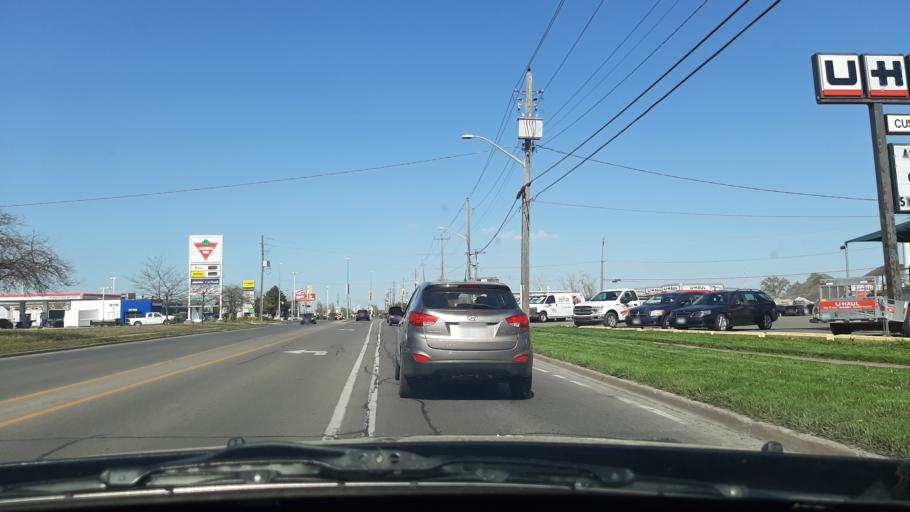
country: CA
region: Ontario
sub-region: Regional Municipality of Niagara
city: St. Catharines
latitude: 43.1741
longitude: -79.2167
